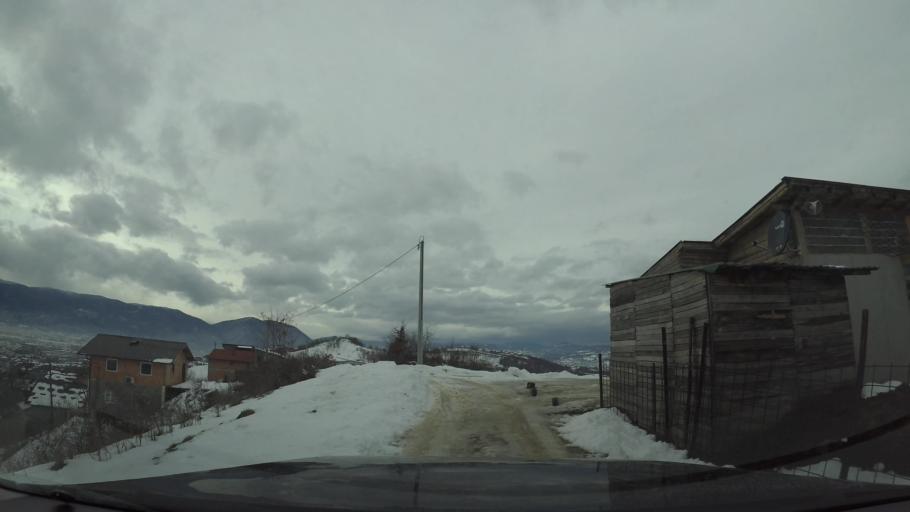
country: BA
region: Federation of Bosnia and Herzegovina
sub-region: Kanton Sarajevo
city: Sarajevo
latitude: 43.8644
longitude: 18.3497
